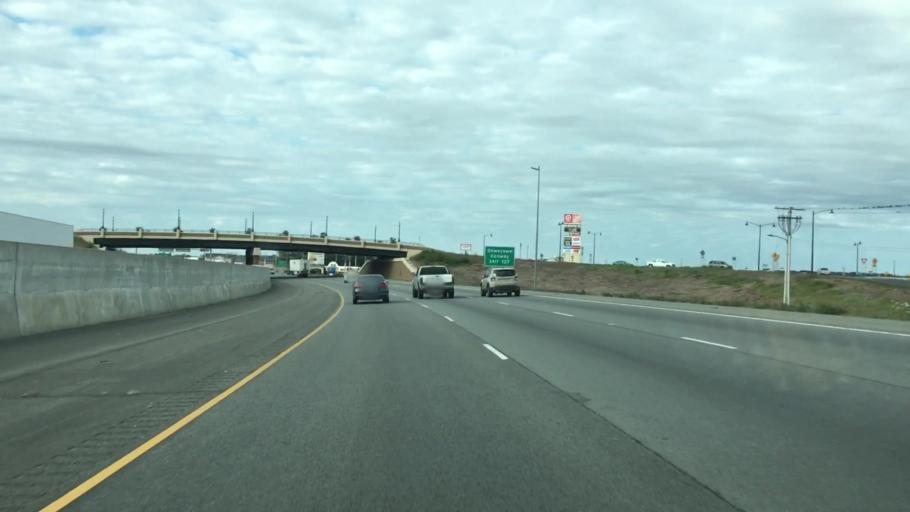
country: US
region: Arkansas
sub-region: Faulkner County
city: Conway
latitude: 35.0829
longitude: -92.4142
